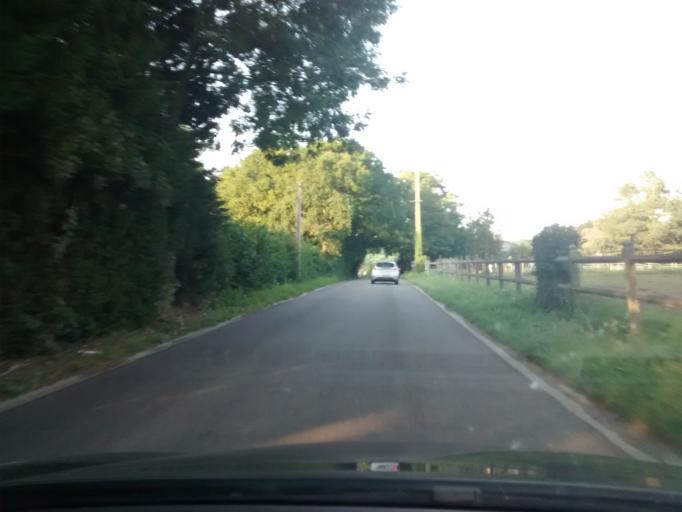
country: FR
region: Lower Normandy
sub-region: Departement du Calvados
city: Blonville-sur-Mer
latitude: 49.3225
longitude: 0.0254
